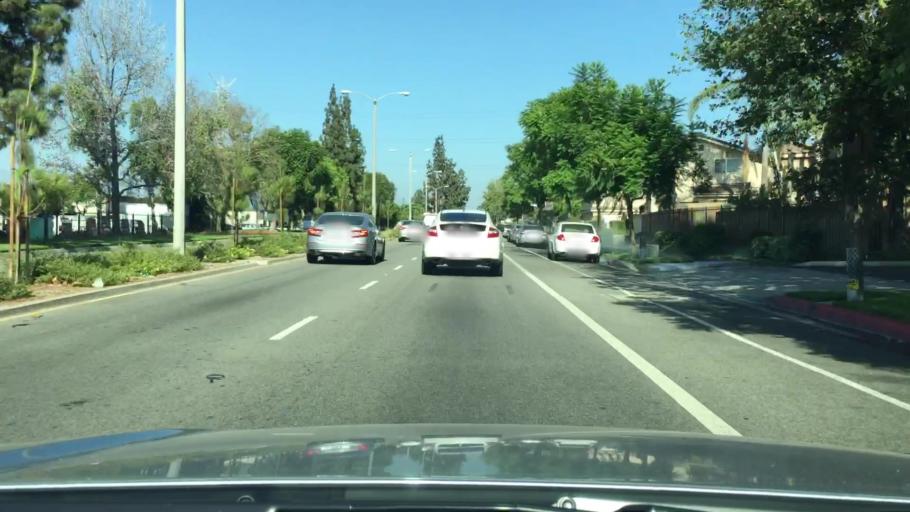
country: US
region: California
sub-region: Los Angeles County
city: Baldwin Park
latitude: 34.0789
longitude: -117.9922
